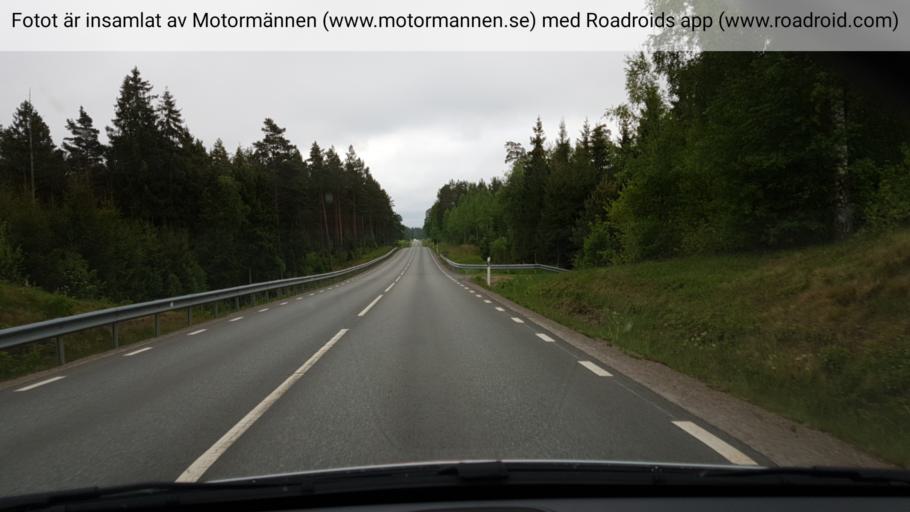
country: SE
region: Joenkoeping
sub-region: Mullsjo Kommun
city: Mullsjoe
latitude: 57.8788
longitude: 13.8522
